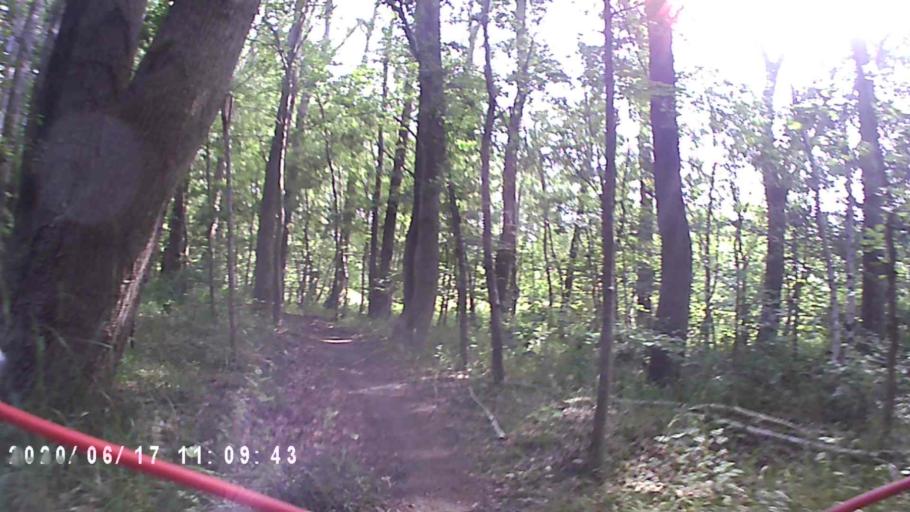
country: NL
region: Friesland
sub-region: Gemeente Dongeradeel
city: Anjum
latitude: 53.3970
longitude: 6.2256
